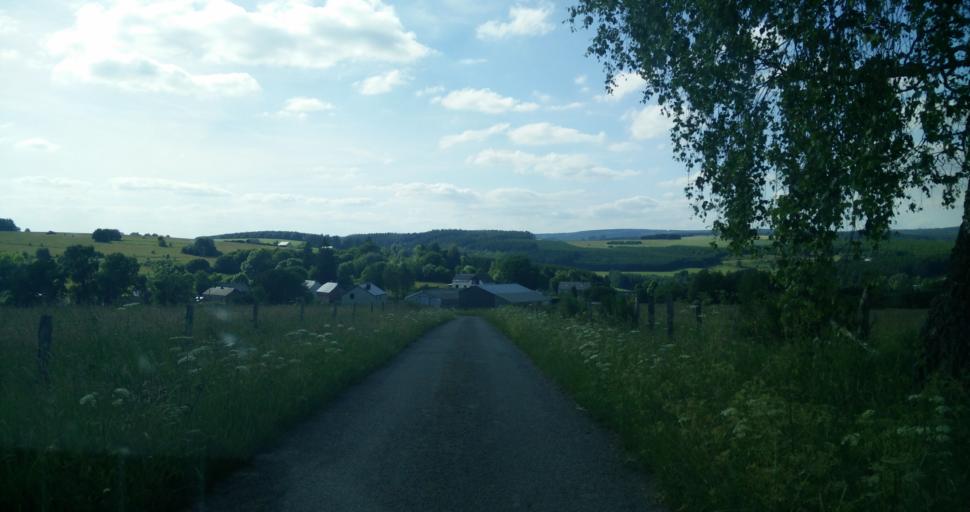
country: BE
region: Wallonia
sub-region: Province du Luxembourg
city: Houffalize
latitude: 50.1447
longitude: 5.7243
